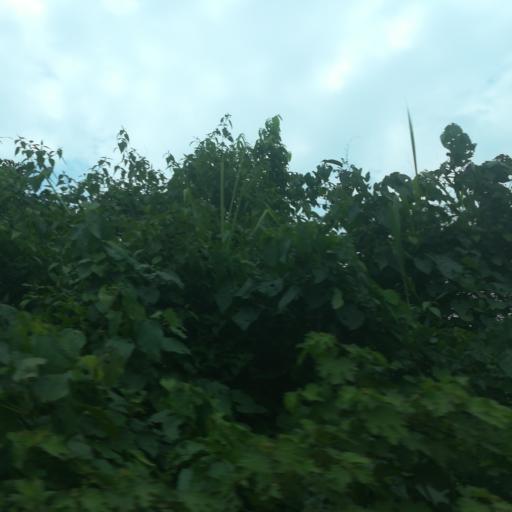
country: NG
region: Lagos
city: Ejirin
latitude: 6.6679
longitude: 3.7939
